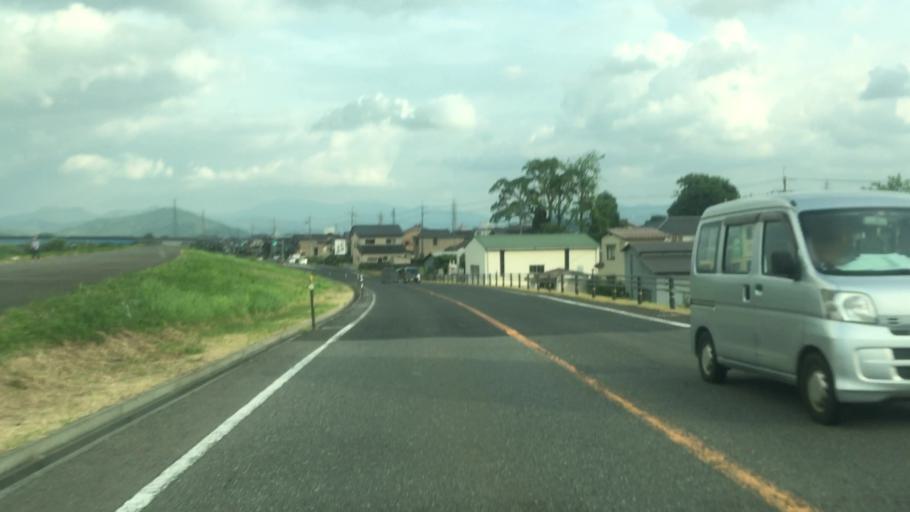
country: JP
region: Hyogo
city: Toyooka
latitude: 35.5606
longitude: 134.8144
